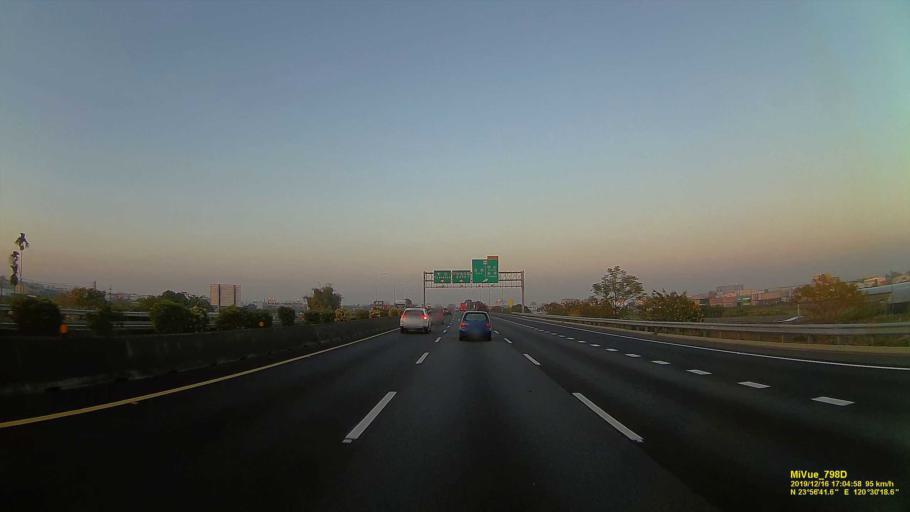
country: TW
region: Taiwan
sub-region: Changhua
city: Chang-hua
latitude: 23.9455
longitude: 120.5053
